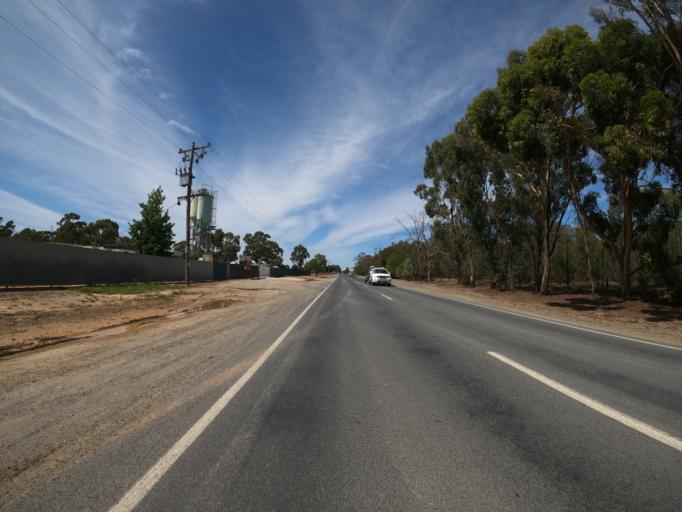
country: AU
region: Victoria
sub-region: Moira
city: Yarrawonga
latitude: -36.0238
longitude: 145.9956
